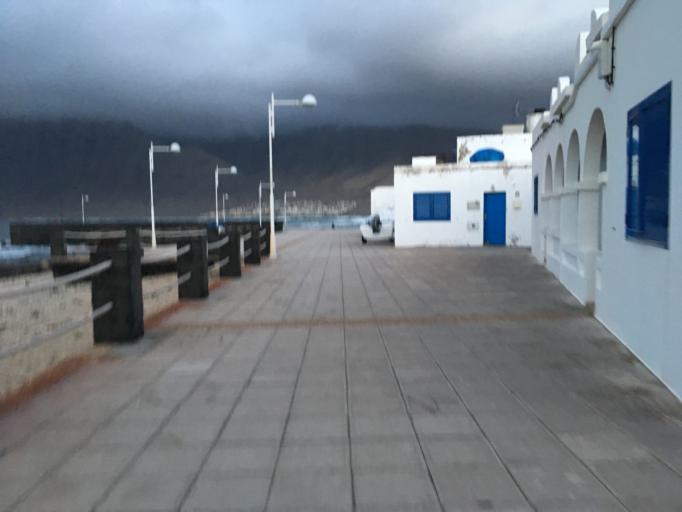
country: ES
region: Canary Islands
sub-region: Provincia de Las Palmas
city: Teguise
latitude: 29.1200
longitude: -13.5668
